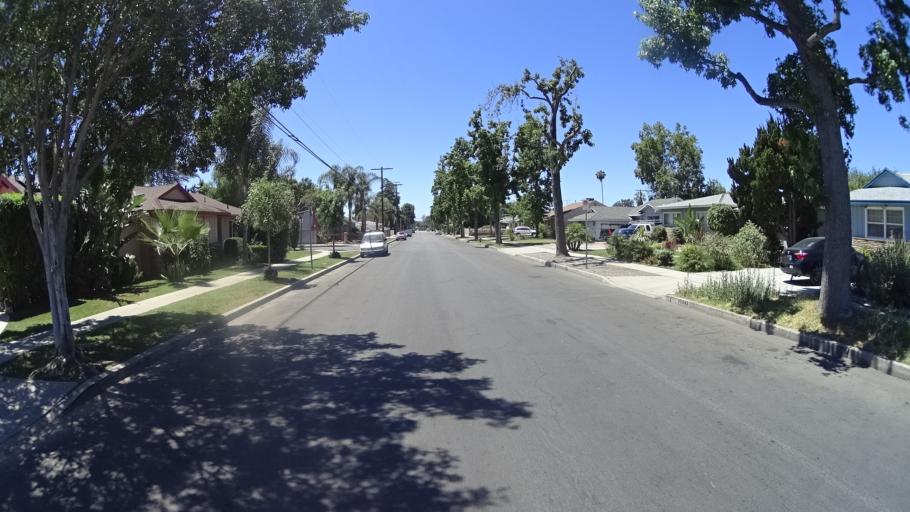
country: US
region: California
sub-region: Los Angeles County
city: San Fernando
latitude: 34.2532
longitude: -118.4697
